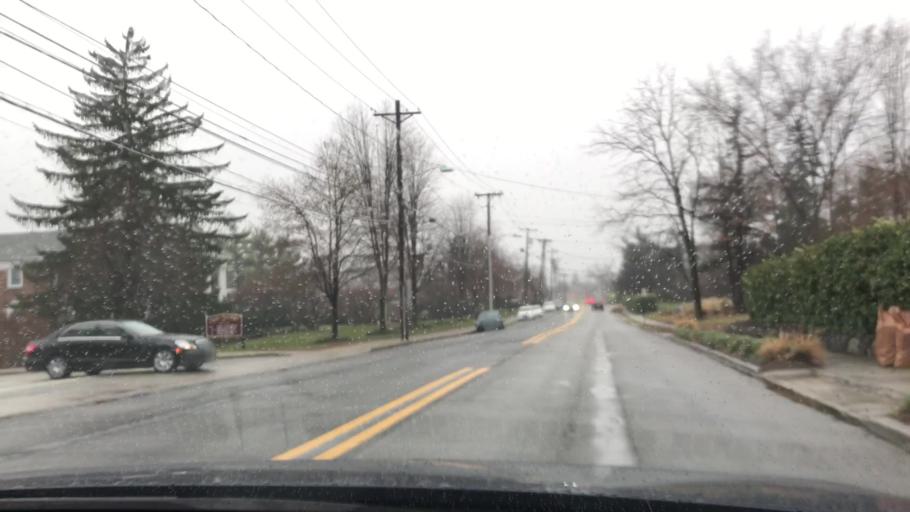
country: US
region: New Jersey
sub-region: Bergen County
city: Ridgewood
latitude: 40.9830
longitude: -74.1125
